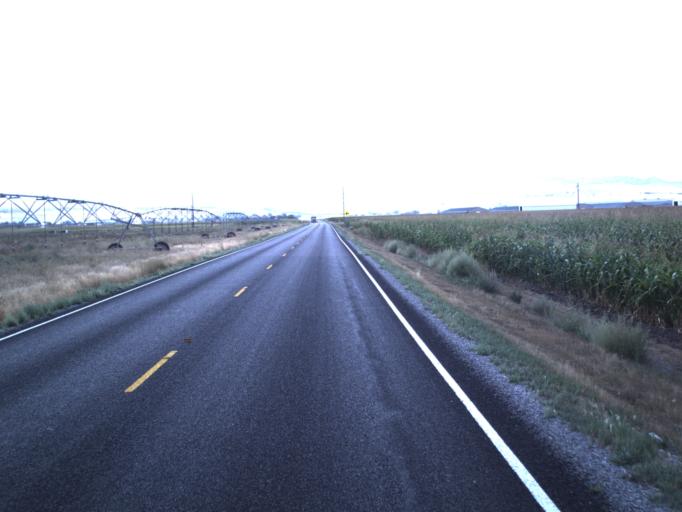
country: US
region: Utah
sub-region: Cache County
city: Lewiston
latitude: 41.9249
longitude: -111.8902
